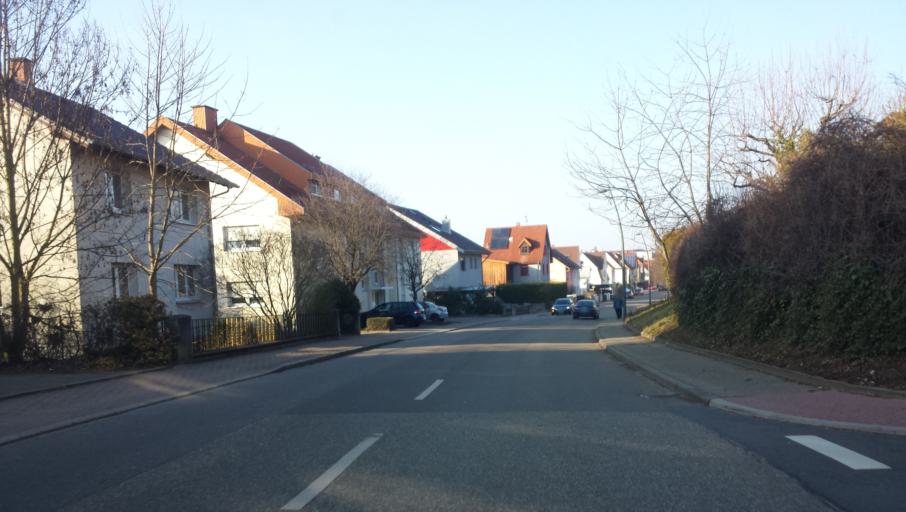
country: DE
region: Baden-Wuerttemberg
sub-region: Karlsruhe Region
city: Nussloch
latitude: 49.3179
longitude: 8.6970
